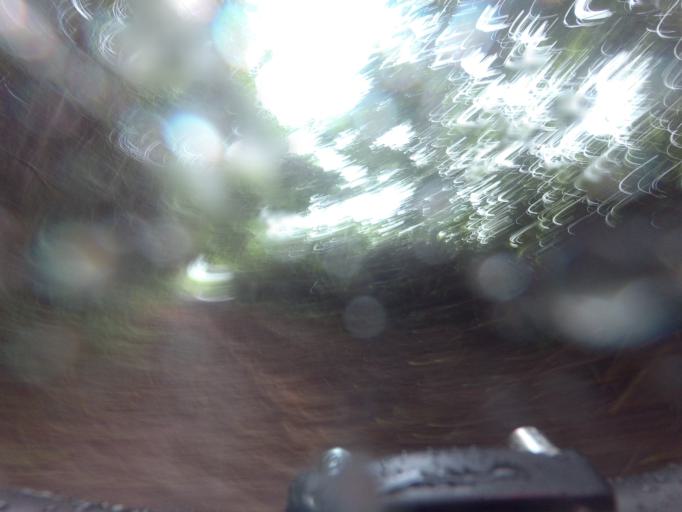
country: CU
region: Pinar del Rio
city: Vinales
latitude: 22.6184
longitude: -83.7164
